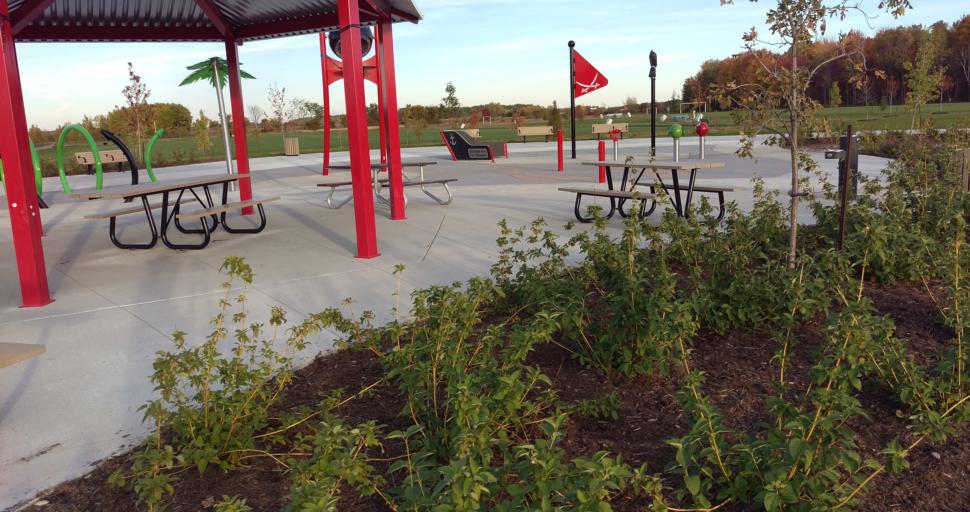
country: CA
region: Ontario
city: Clarence-Rockland
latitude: 45.4661
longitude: -75.4468
